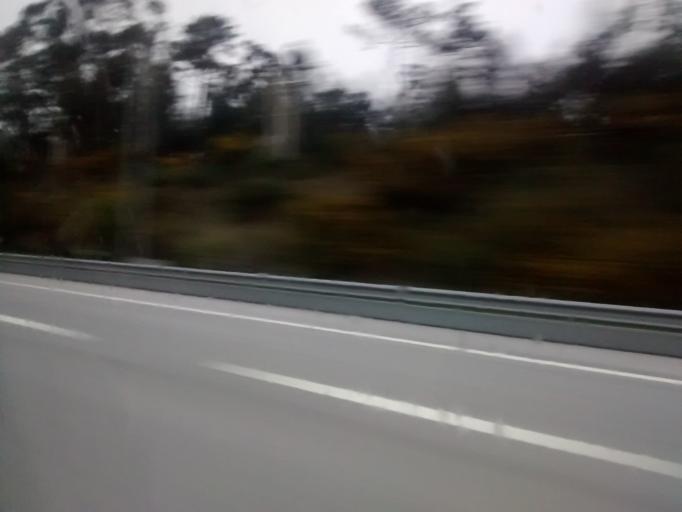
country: PT
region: Aveiro
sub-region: Estarreja
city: Salreu
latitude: 40.6907
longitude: -8.5487
